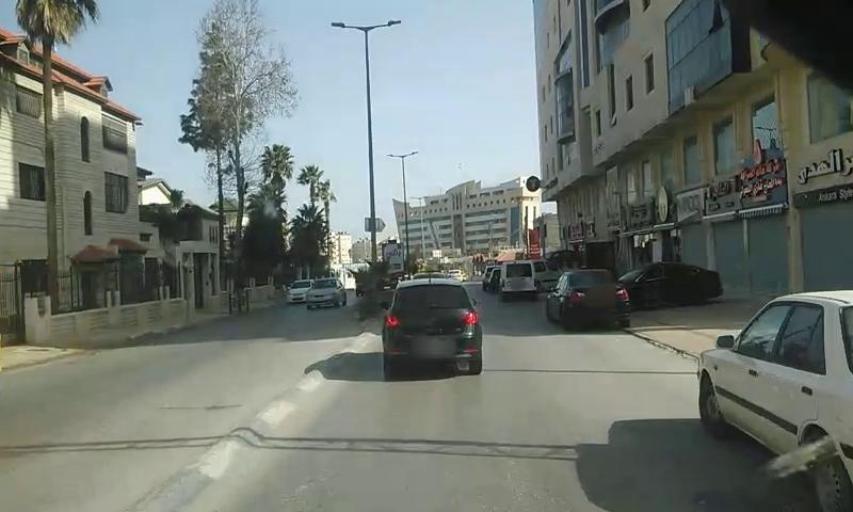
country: PS
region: West Bank
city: Surda
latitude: 31.9239
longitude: 35.2087
